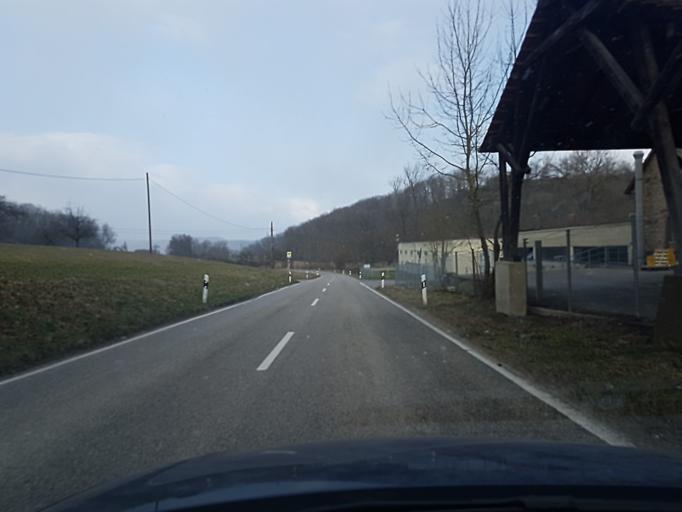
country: DE
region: Baden-Wuerttemberg
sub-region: Regierungsbezirk Stuttgart
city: Eberdingen
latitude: 48.9043
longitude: 8.9776
